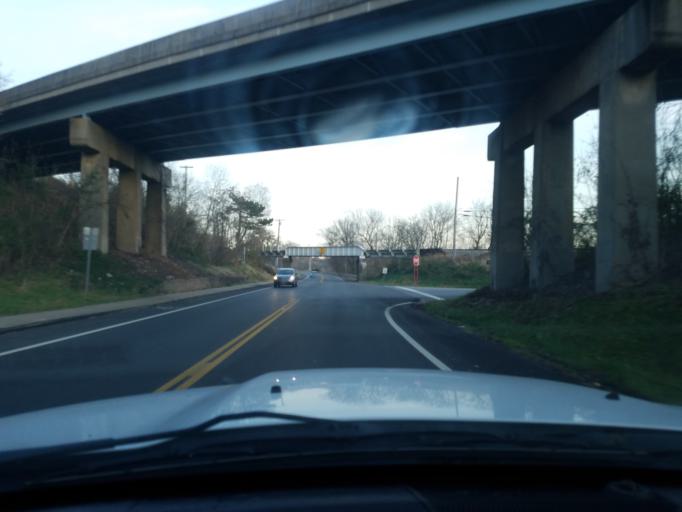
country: US
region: Ohio
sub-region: Washington County
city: Marietta
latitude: 39.4046
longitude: -81.4712
